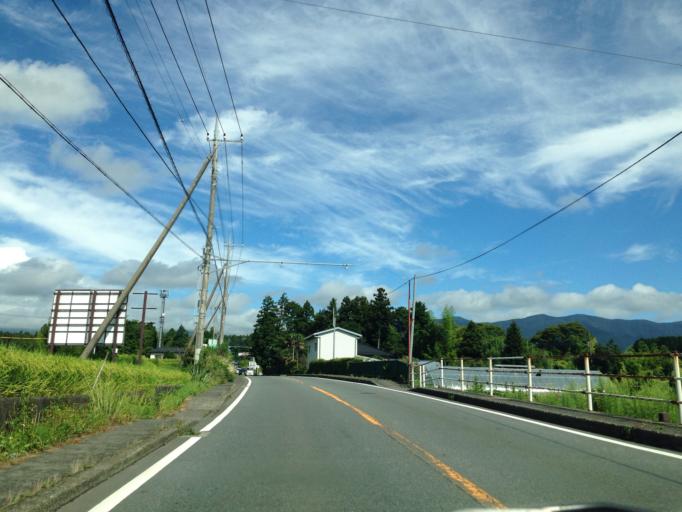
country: JP
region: Shizuoka
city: Gotemba
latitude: 35.3200
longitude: 138.9135
